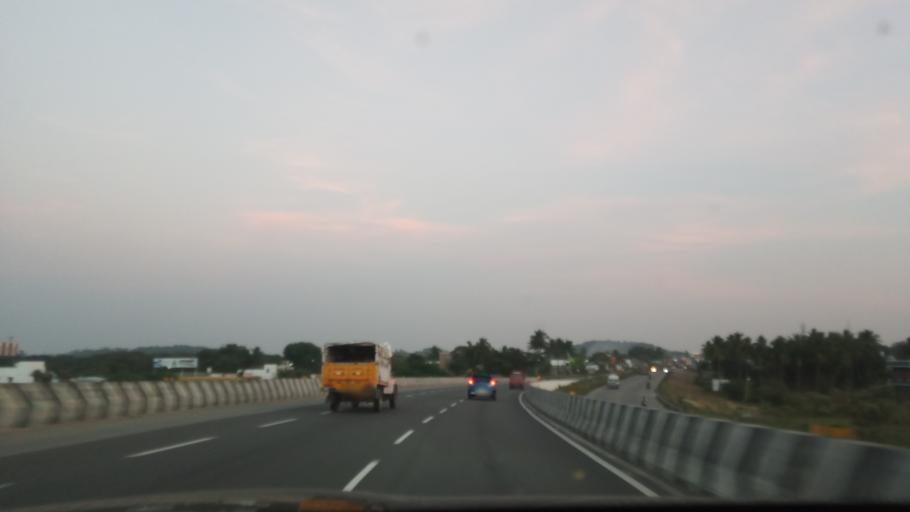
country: IN
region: Tamil Nadu
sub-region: Vellore
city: Walajapet
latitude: 12.9167
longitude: 79.3877
